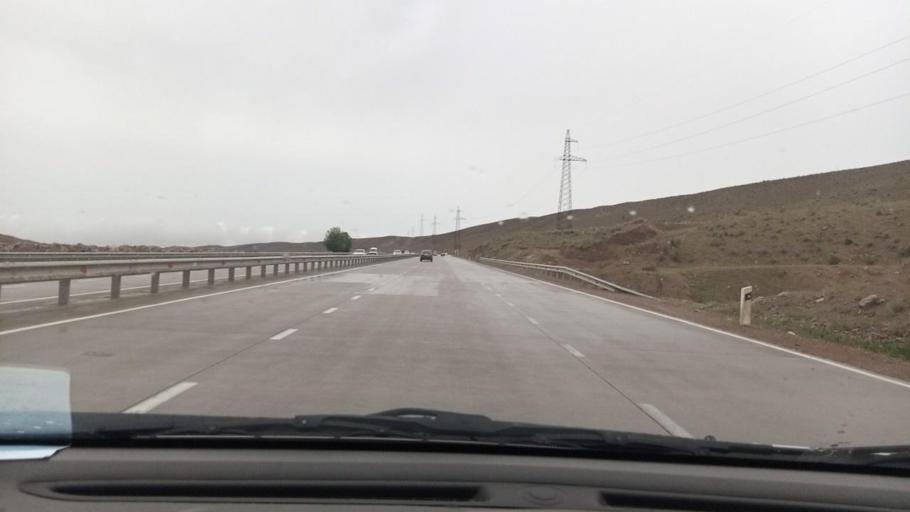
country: UZ
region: Namangan
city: Pop Shahri
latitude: 40.9388
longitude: 70.6923
